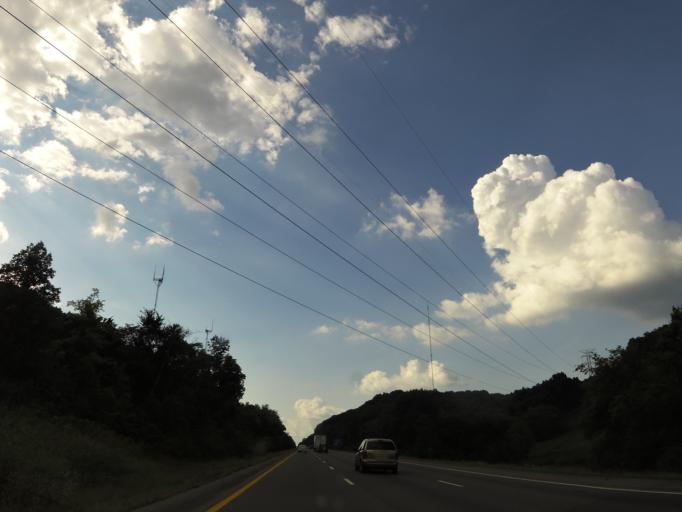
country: US
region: Tennessee
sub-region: Davidson County
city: Nashville
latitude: 36.2557
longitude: -86.7863
